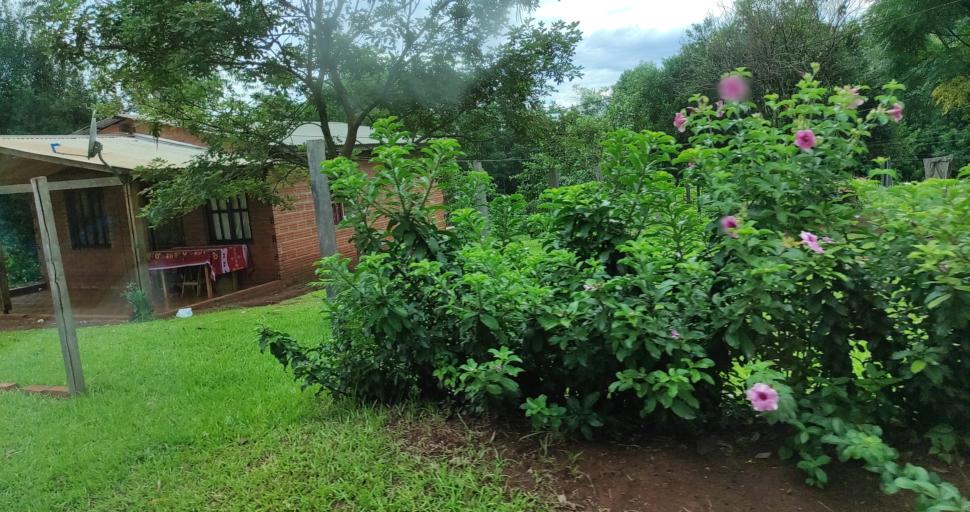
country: AR
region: Misiones
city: Puerto Libertad
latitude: -25.9635
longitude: -54.5941
